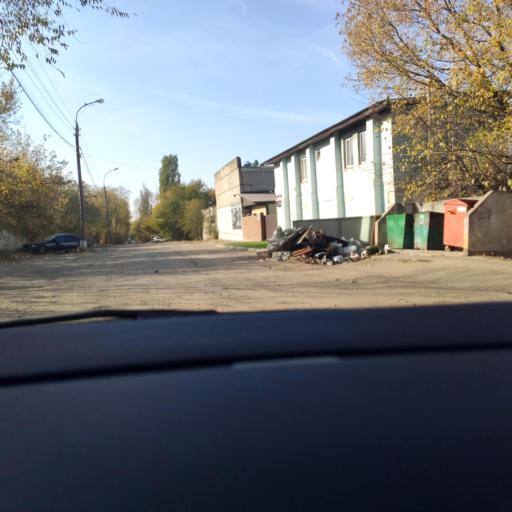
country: RU
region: Voronezj
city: Voronezh
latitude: 51.6913
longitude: 39.1700
